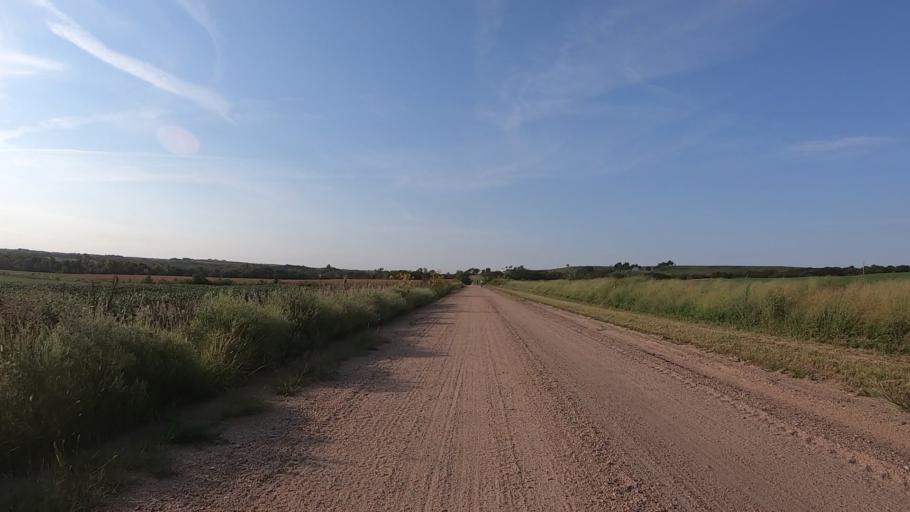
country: US
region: Kansas
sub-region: Marshall County
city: Blue Rapids
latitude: 39.6948
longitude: -96.7792
